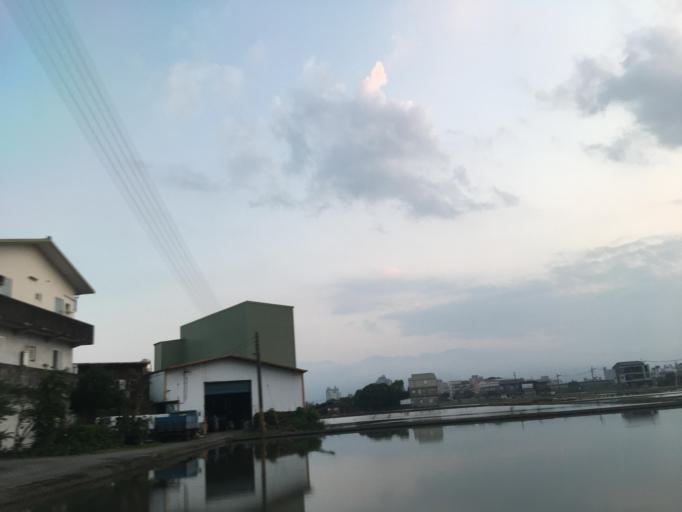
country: TW
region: Taiwan
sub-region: Yilan
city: Yilan
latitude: 24.6927
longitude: 121.7779
